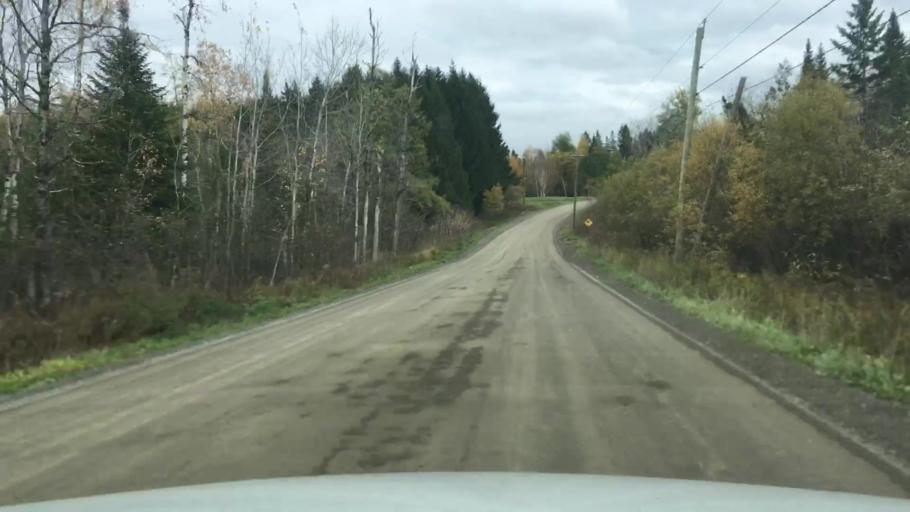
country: US
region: Maine
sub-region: Aroostook County
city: Easton
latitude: 46.5219
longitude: -67.8902
